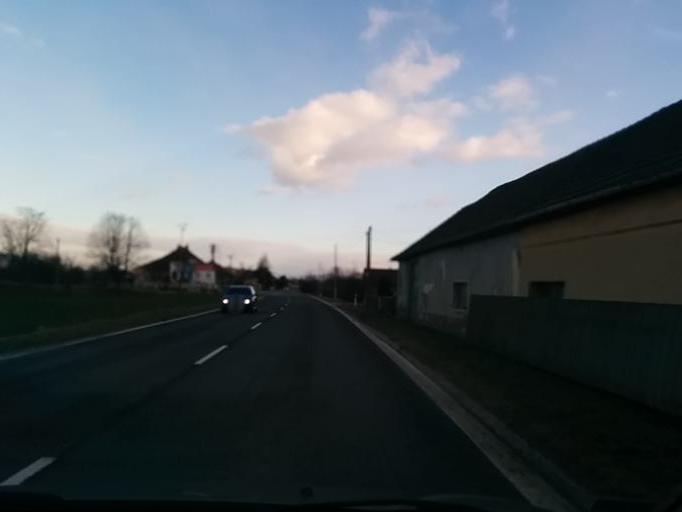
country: SK
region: Nitriansky
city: Cachtice
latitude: 48.6821
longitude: 17.8473
